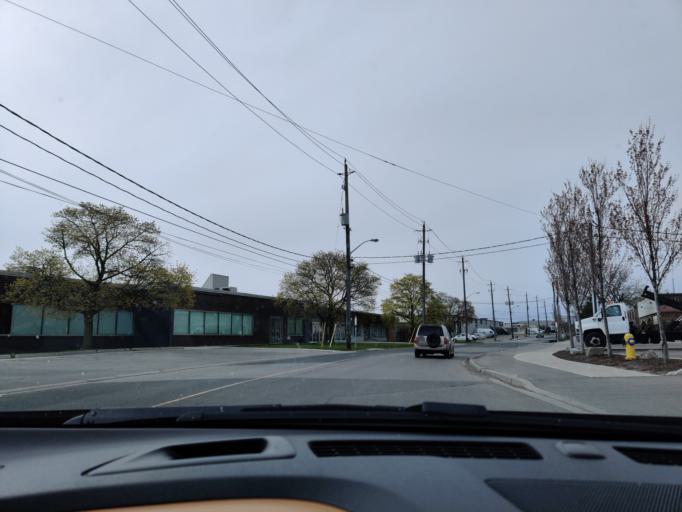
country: CA
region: Ontario
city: Toronto
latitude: 43.7030
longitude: -79.4697
